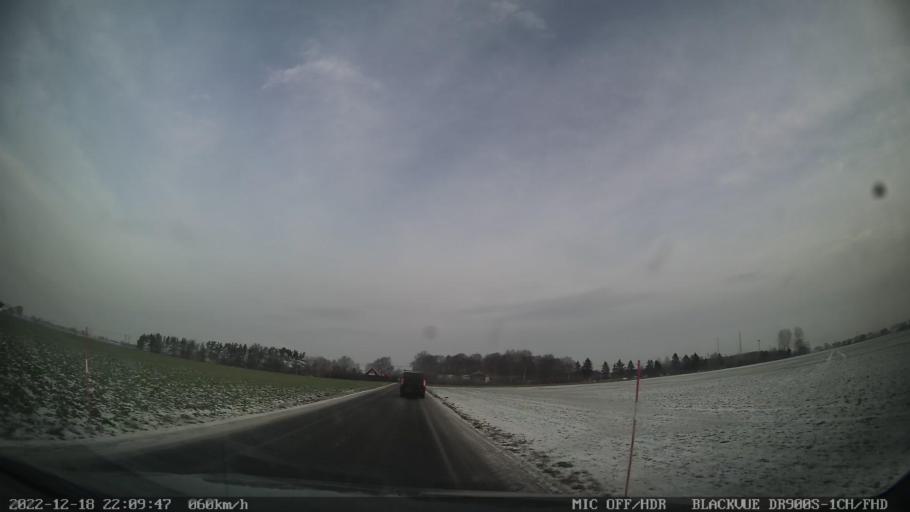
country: SE
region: Skane
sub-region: Tomelilla Kommun
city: Tomelilla
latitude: 55.5368
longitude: 14.0416
